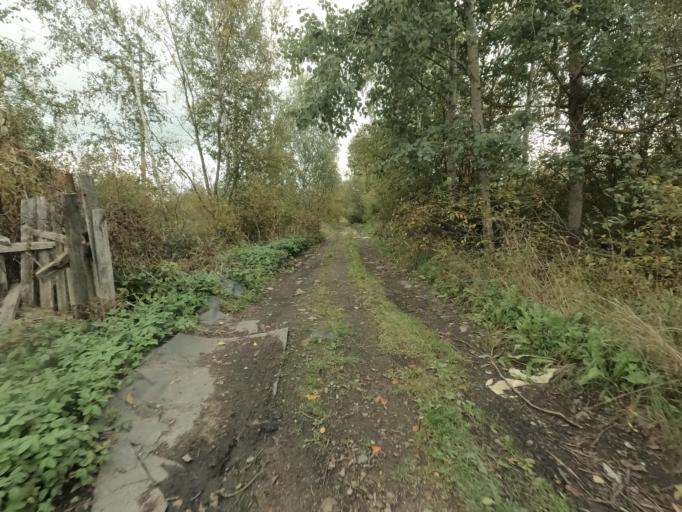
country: RU
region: St.-Petersburg
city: Sapernyy
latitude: 59.7777
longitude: 30.6411
